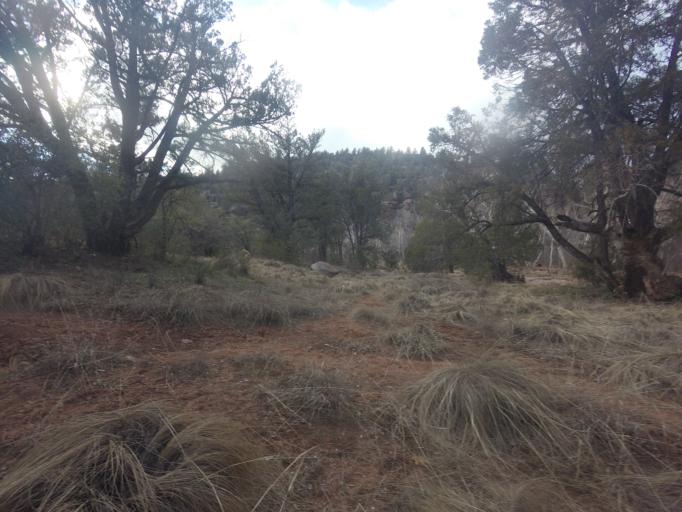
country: US
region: Arizona
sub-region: Gila County
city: Payson
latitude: 34.3039
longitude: -111.3522
